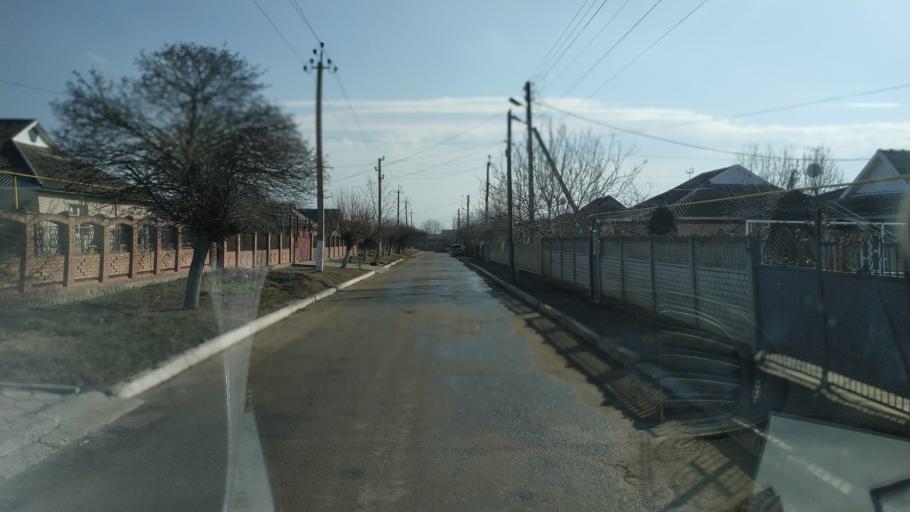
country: MD
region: Chisinau
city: Singera
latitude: 46.6839
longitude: 29.0610
